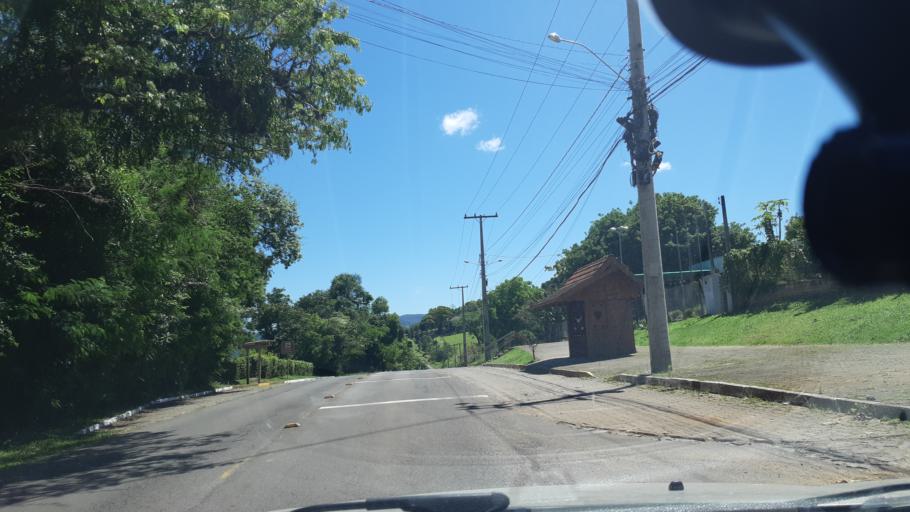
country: BR
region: Rio Grande do Sul
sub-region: Novo Hamburgo
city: Novo Hamburgo
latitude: -29.6242
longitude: -51.0938
